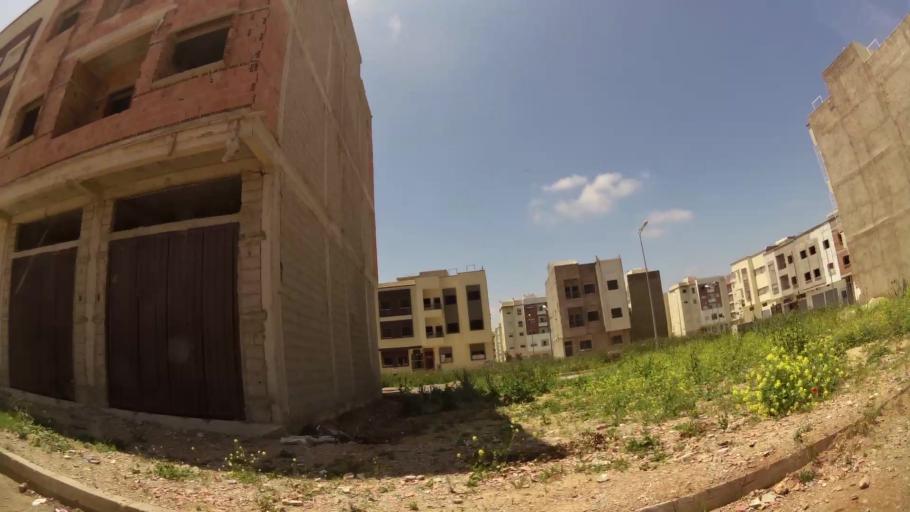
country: MA
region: Fes-Boulemane
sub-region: Fes
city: Fes
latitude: 34.0321
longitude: -5.0546
